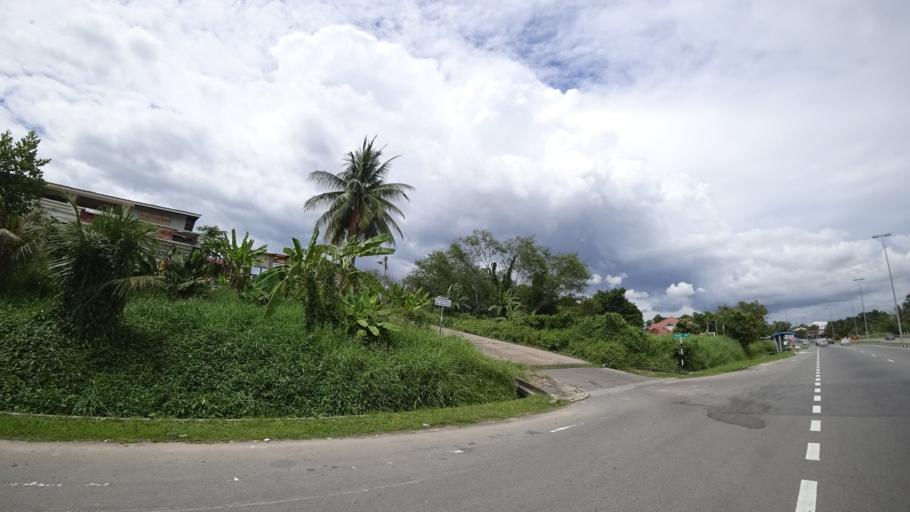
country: BN
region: Brunei and Muara
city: Bandar Seri Begawan
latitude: 4.8783
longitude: 114.8617
